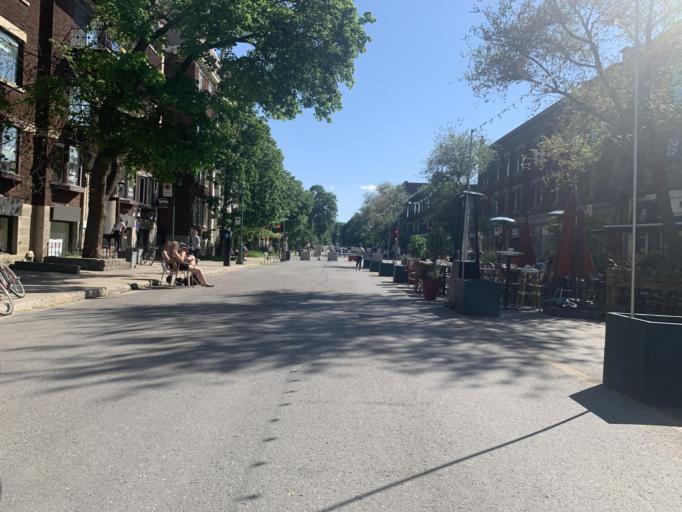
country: CA
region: Quebec
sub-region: Montreal
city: Montreal
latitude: 45.5198
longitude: -73.6090
